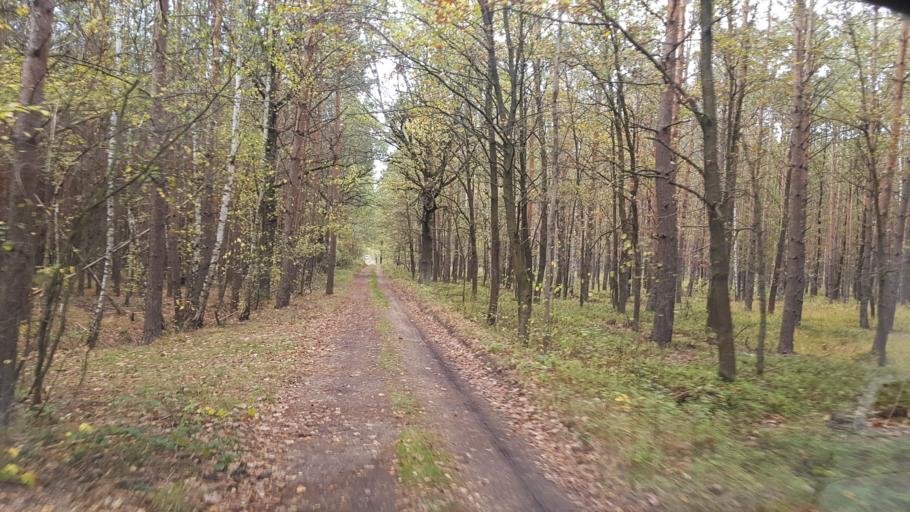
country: DE
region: Brandenburg
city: Schonborn
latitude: 51.6465
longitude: 13.5089
